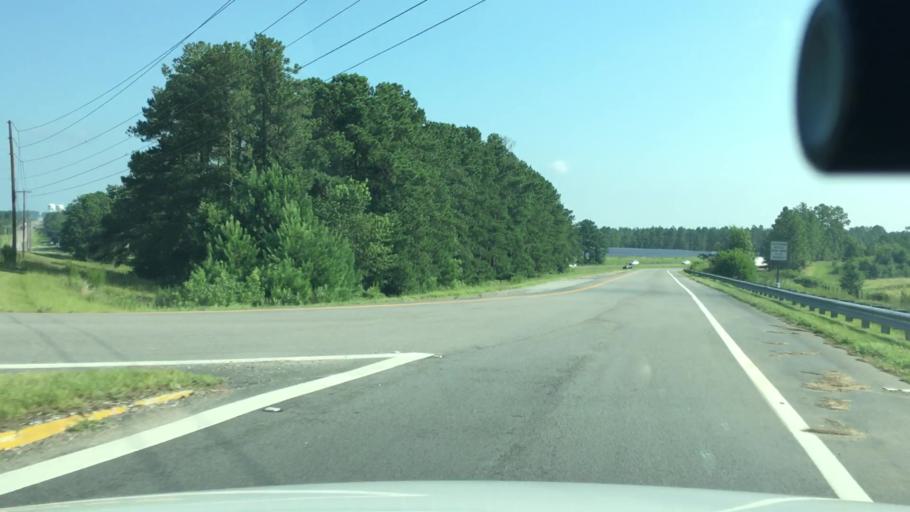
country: US
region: South Carolina
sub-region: Aiken County
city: Graniteville
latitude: 33.6047
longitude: -81.8427
